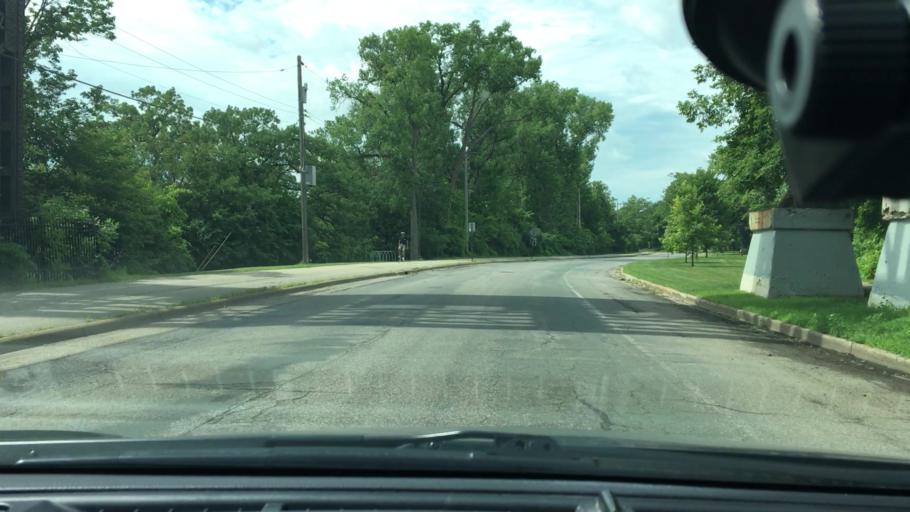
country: US
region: Minnesota
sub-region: Ramsey County
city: Lauderdale
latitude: 44.9569
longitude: -93.2111
